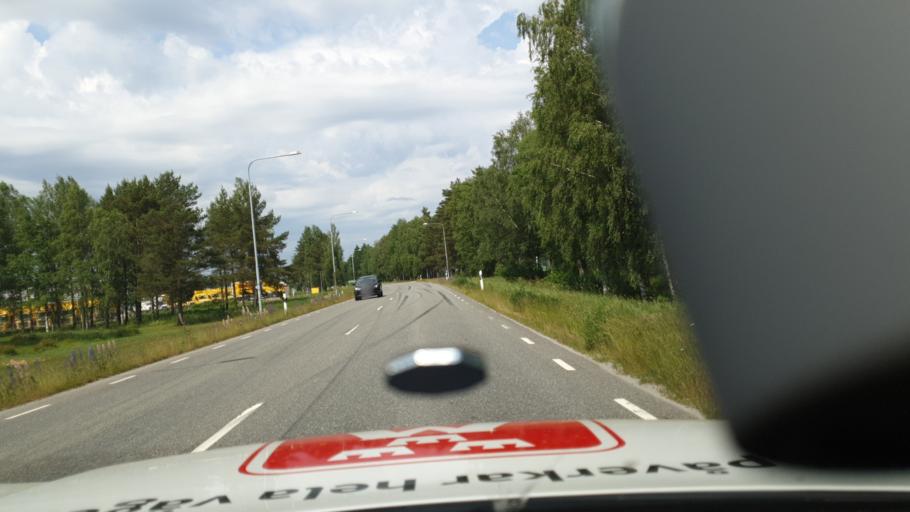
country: SE
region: Joenkoeping
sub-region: Varnamo Kommun
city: Varnamo
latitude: 57.2119
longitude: 14.0398
